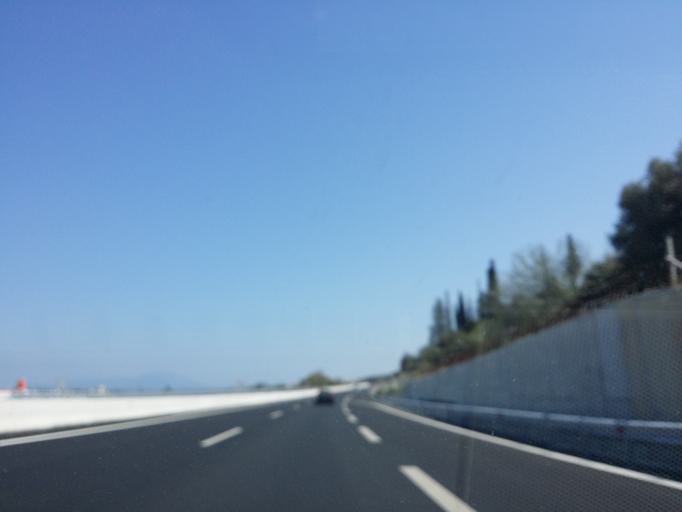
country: GR
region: Peloponnese
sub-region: Nomos Korinthias
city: Xylokastro
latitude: 38.0703
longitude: 22.6373
